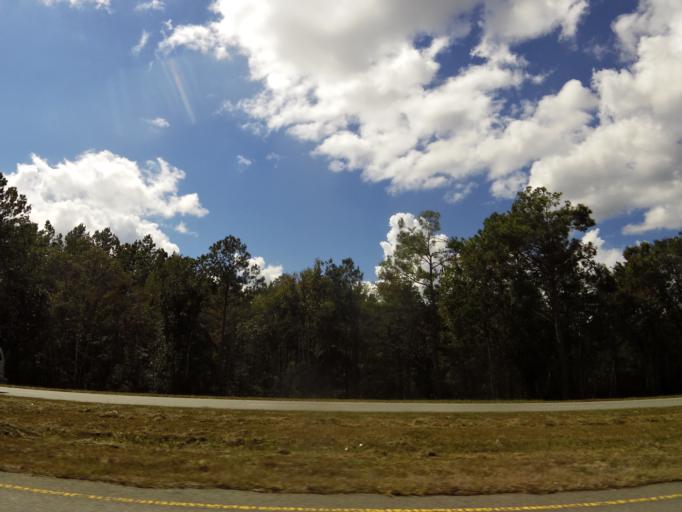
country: US
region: Georgia
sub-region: Charlton County
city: Folkston
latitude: 30.8012
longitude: -81.9896
